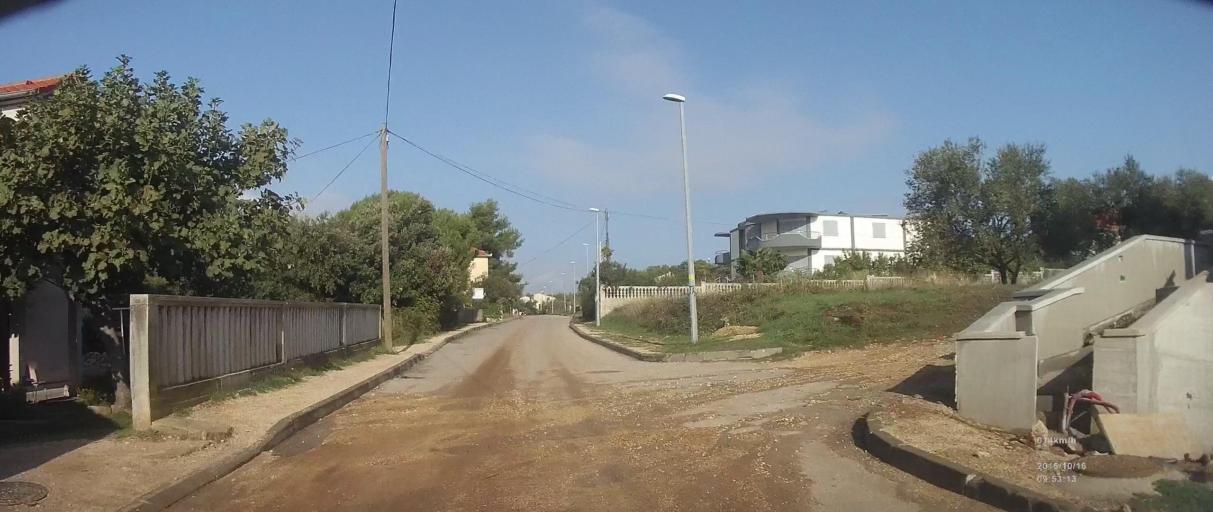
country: HR
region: Zadarska
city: Pakostane
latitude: 43.9115
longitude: 15.5039
